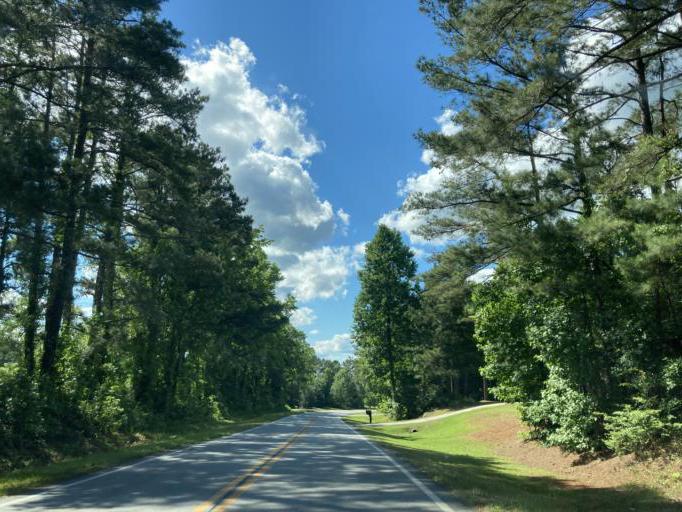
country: US
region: Georgia
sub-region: Jones County
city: Gray
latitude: 32.9799
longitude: -83.5477
